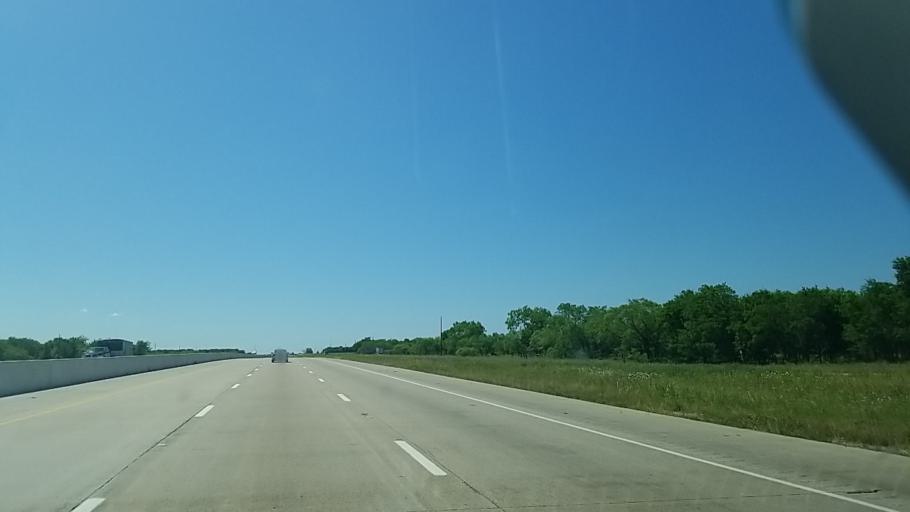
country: US
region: Texas
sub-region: Freestone County
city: Wortham
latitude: 31.8977
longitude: -96.3703
